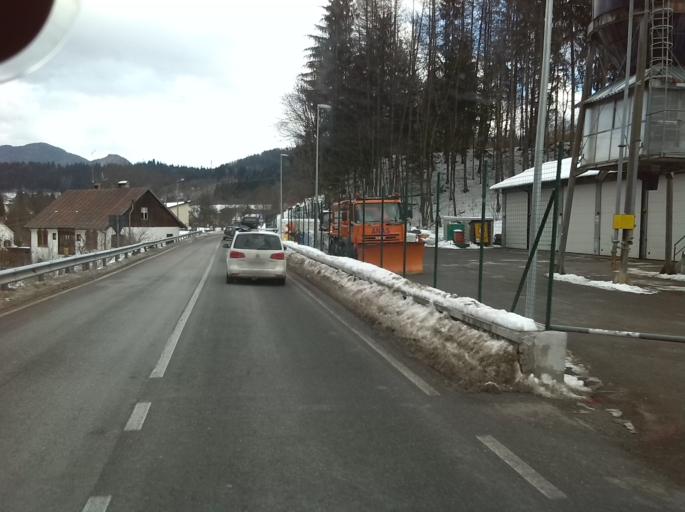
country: IT
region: Friuli Venezia Giulia
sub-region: Provincia di Udine
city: Tarvisio
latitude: 46.5038
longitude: 13.5888
